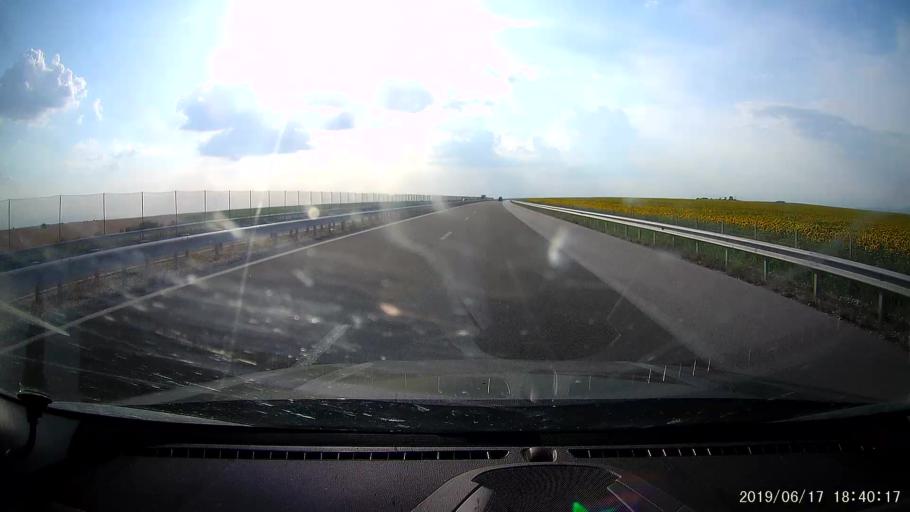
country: BG
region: Stara Zagora
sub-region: Obshtina Chirpan
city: Chirpan
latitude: 42.1536
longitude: 25.2821
